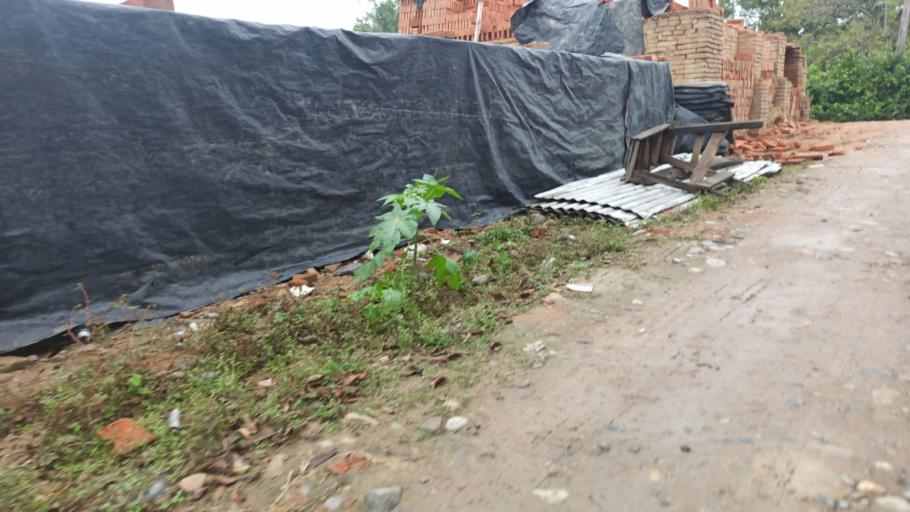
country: MX
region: Veracruz
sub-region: Papantla
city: El Chote
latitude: 20.3734
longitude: -97.3354
